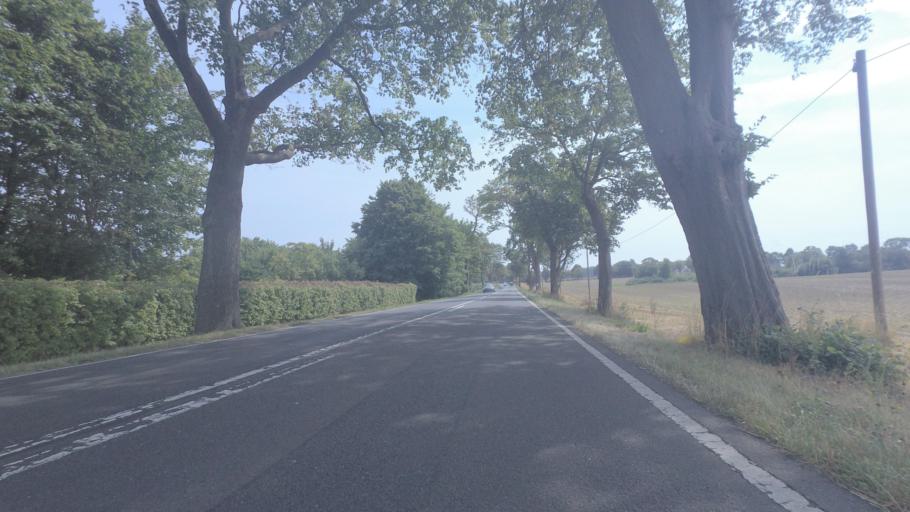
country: DE
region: Mecklenburg-Vorpommern
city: Garz
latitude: 54.3203
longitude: 13.3377
